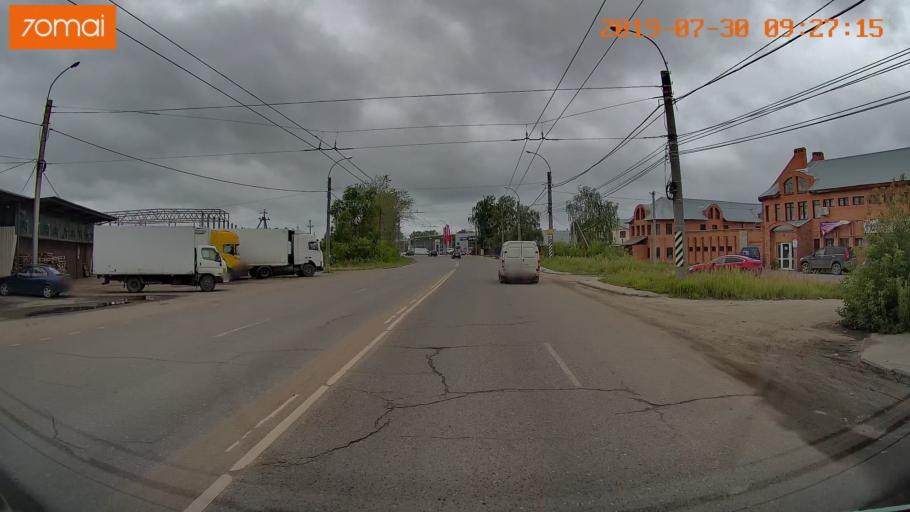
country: RU
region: Ivanovo
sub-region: Gorod Ivanovo
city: Ivanovo
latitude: 56.9466
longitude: 40.9717
